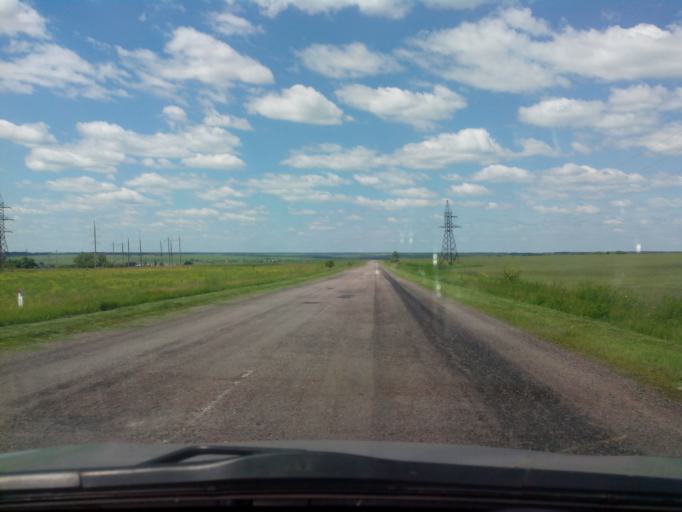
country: RU
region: Voronezj
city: Ternovka
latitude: 51.5909
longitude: 41.8157
